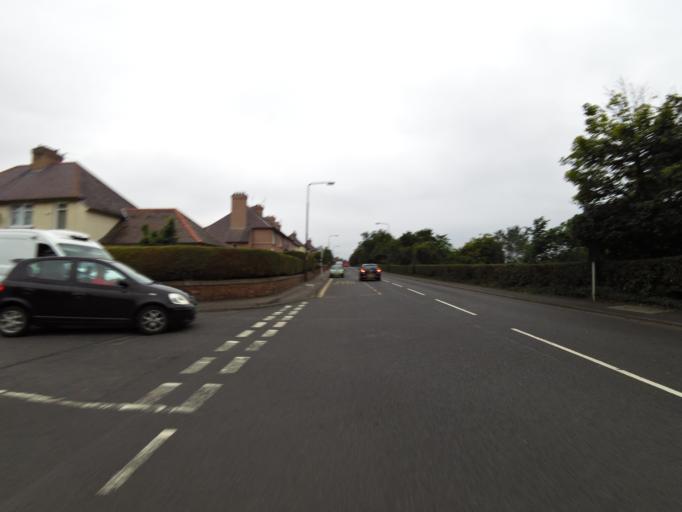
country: GB
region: Scotland
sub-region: East Lothian
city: Musselburgh
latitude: 55.9329
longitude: -3.0600
